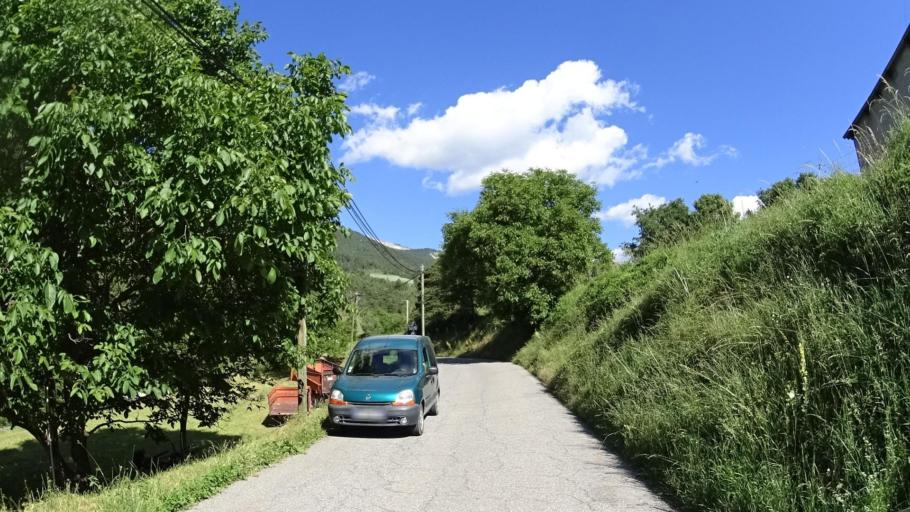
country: FR
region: Provence-Alpes-Cote d'Azur
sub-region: Departement des Alpes-de-Haute-Provence
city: Annot
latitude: 44.0052
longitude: 6.6390
